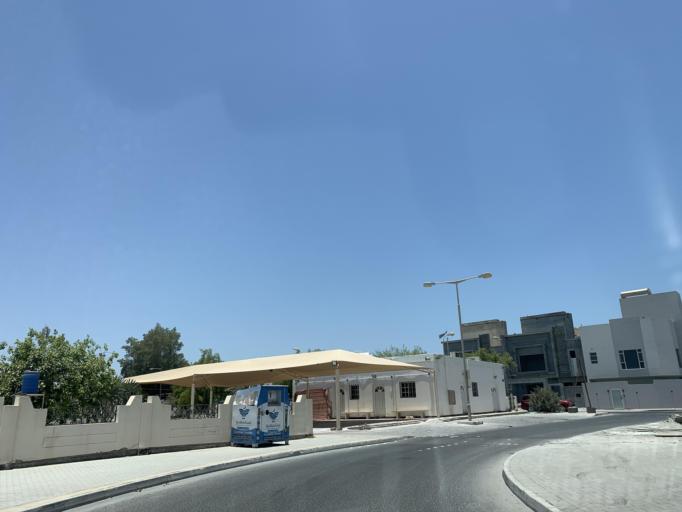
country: BH
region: Manama
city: Jidd Hafs
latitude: 26.2296
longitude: 50.4840
